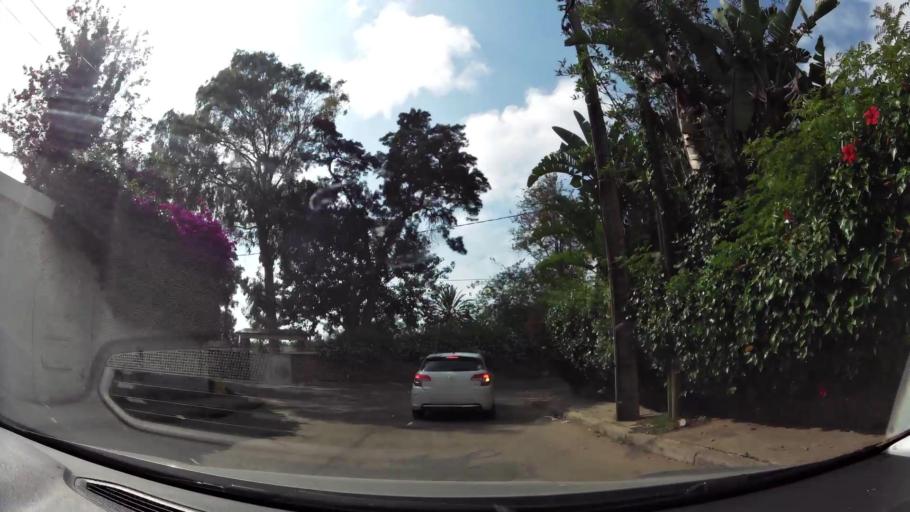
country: MA
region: Rabat-Sale-Zemmour-Zaer
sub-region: Rabat
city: Rabat
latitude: 33.9738
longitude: -6.8474
